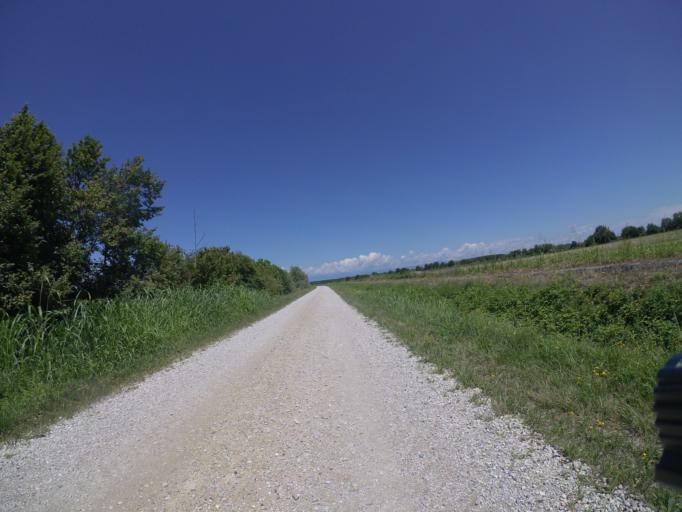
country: IT
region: Friuli Venezia Giulia
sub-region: Provincia di Udine
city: Teor
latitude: 45.8853
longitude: 13.0901
